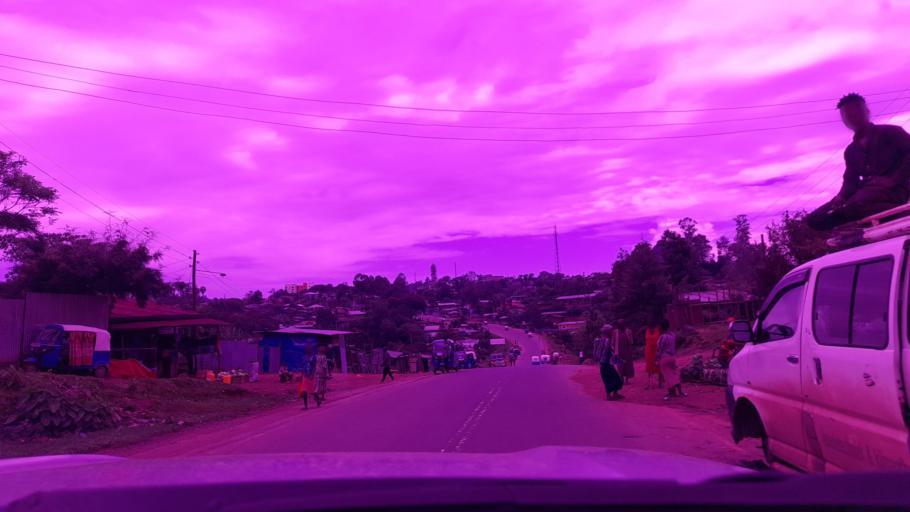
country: ET
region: Southern Nations, Nationalities, and People's Region
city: Mizan Teferi
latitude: 7.0015
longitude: 35.5979
